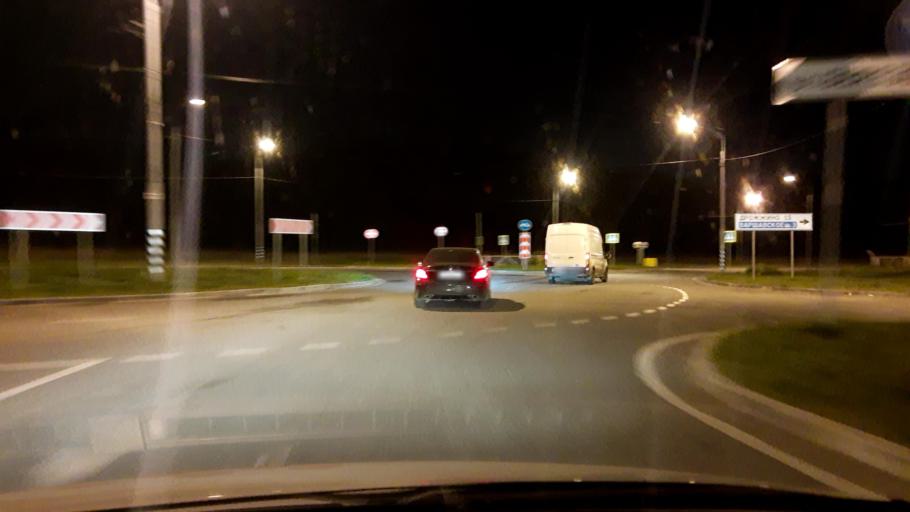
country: RU
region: Moscow
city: Annino
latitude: 55.5261
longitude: 37.6244
